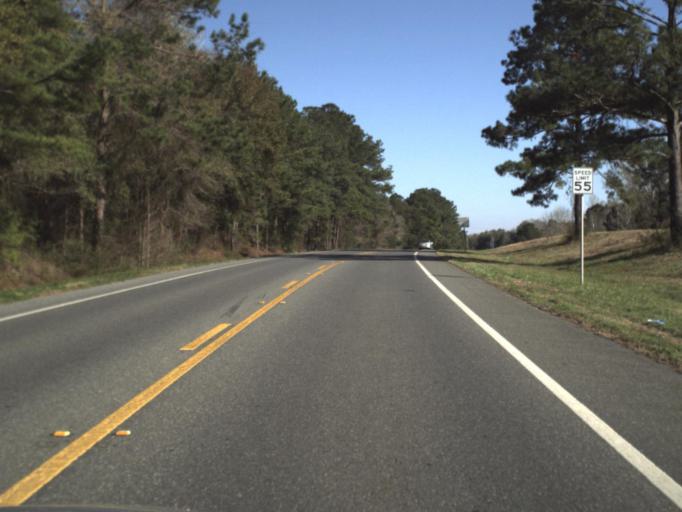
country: US
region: Florida
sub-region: Jackson County
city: Marianna
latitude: 30.7914
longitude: -85.3616
